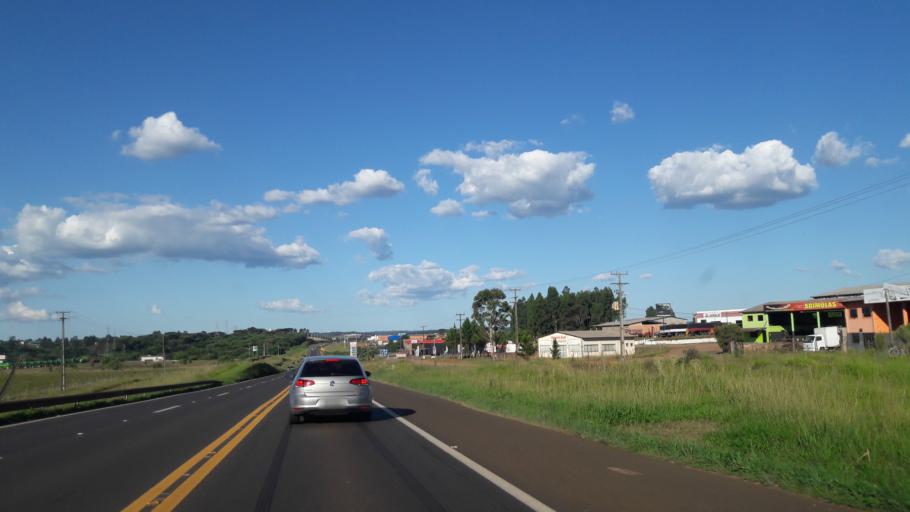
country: BR
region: Parana
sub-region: Guarapuava
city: Guarapuava
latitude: -25.3781
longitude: -51.5062
